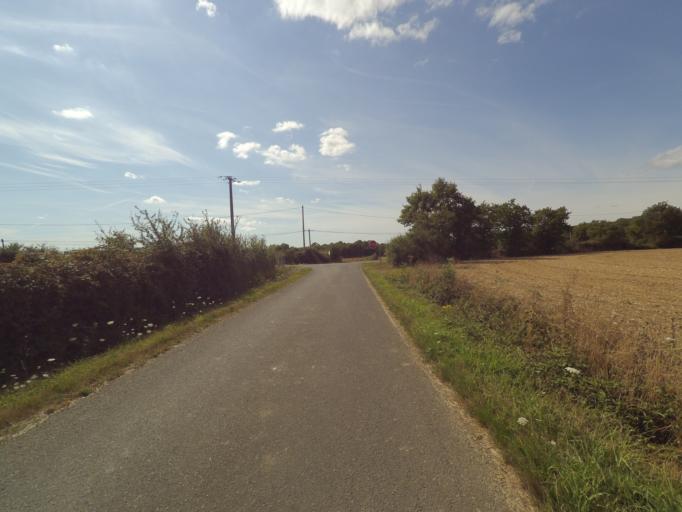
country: FR
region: Pays de la Loire
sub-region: Departement de la Loire-Atlantique
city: Vieillevigne
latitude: 46.9557
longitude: -1.4525
